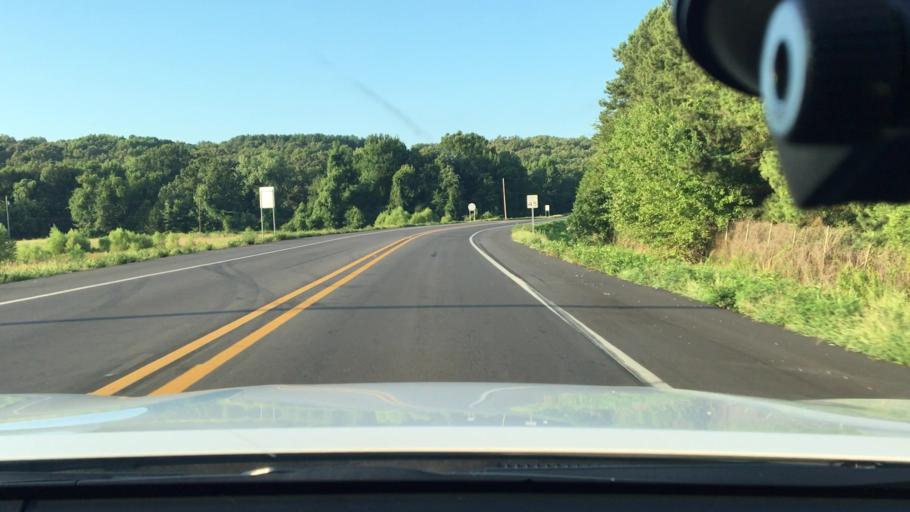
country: US
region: Arkansas
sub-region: Johnson County
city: Clarksville
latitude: 35.4245
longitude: -93.5296
